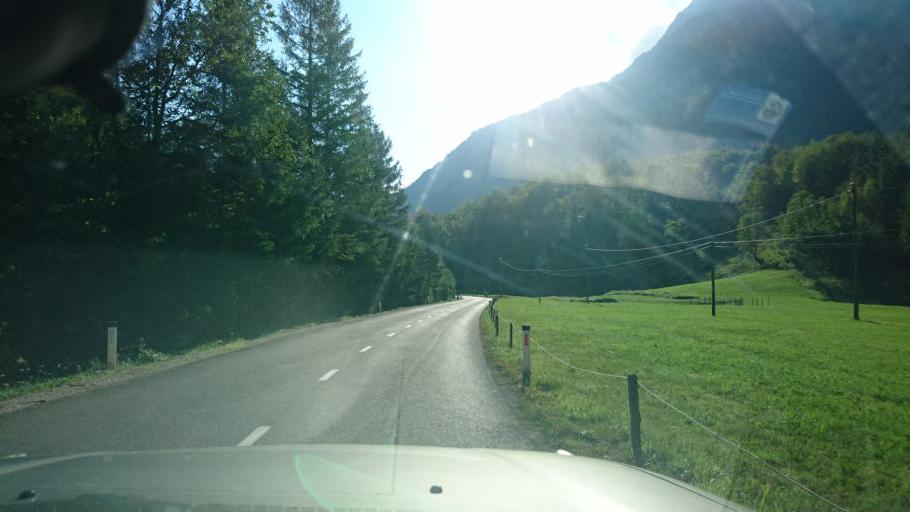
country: SI
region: Kranjska Gora
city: Kranjska Gora
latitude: 46.3600
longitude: 13.7079
